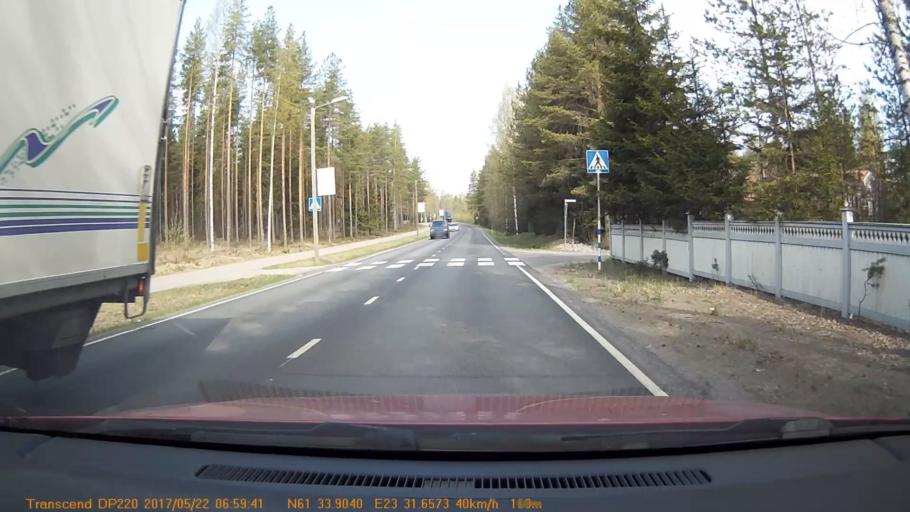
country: FI
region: Pirkanmaa
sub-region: Tampere
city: Yloejaervi
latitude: 61.5654
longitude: 23.5269
